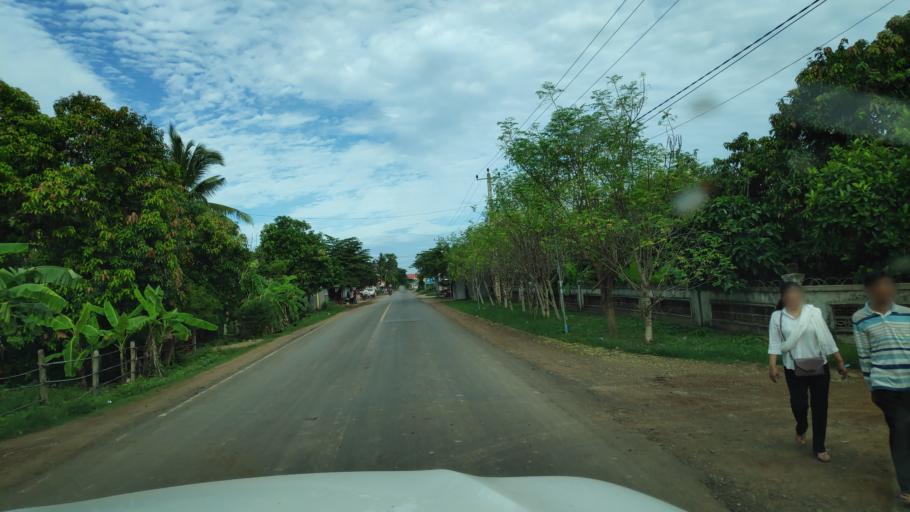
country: KH
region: Kampong Cham
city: Kampong Cham
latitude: 11.9465
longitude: 105.2494
